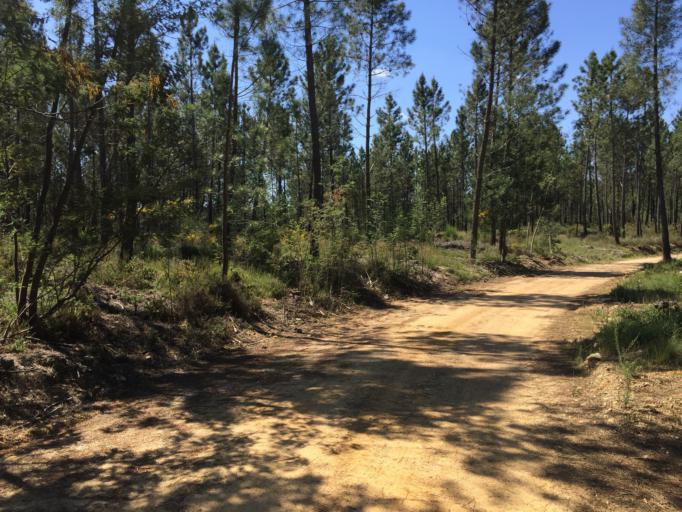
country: PT
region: Coimbra
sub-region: Pampilhosa da Serra
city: Pampilhosa da Serra
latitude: 40.0781
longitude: -7.7786
